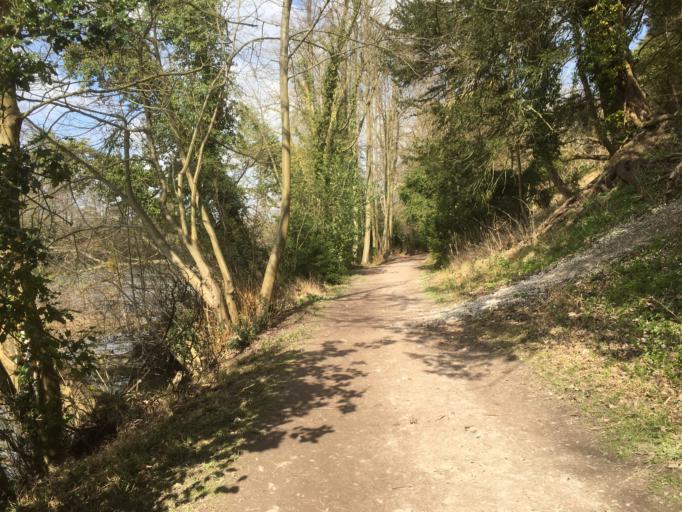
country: GB
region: England
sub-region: Royal Borough of Windsor and Maidenhead
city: Cookham
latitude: 51.5507
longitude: -0.6908
